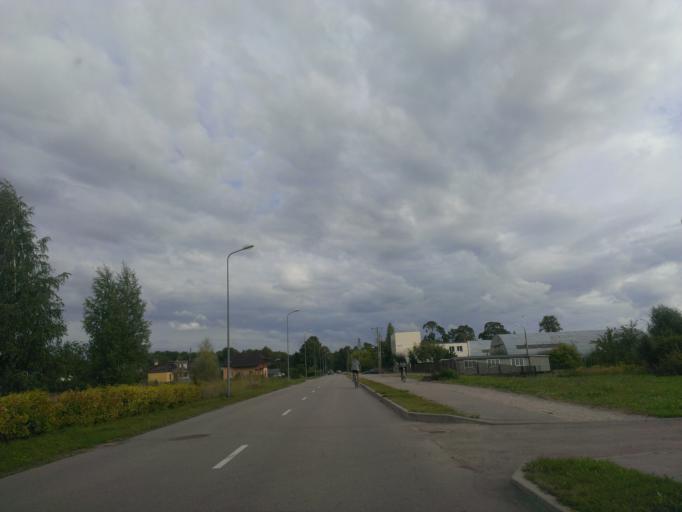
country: LV
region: Ikskile
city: Ikskile
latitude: 56.8332
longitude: 24.4820
